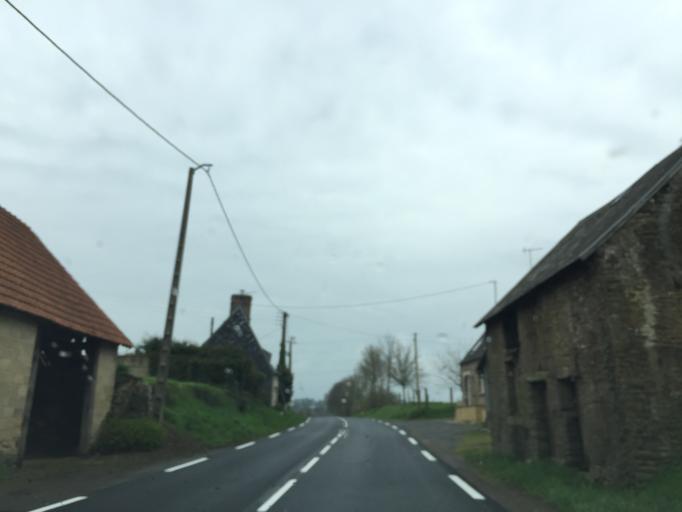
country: FR
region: Lower Normandy
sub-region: Departement de la Manche
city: Saint-James
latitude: 48.5346
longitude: -1.3518
